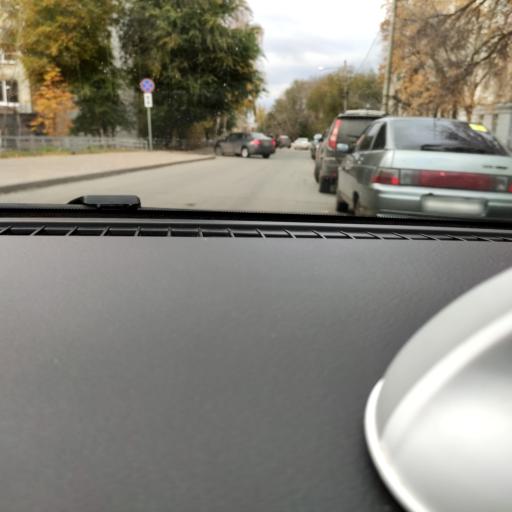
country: RU
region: Samara
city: Samara
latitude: 53.2089
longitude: 50.1238
